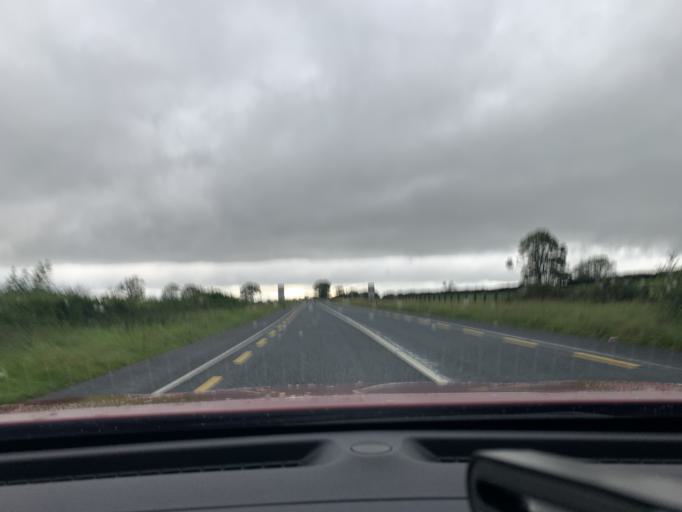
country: IE
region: Connaught
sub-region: Sligo
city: Sligo
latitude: 54.2925
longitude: -8.4868
